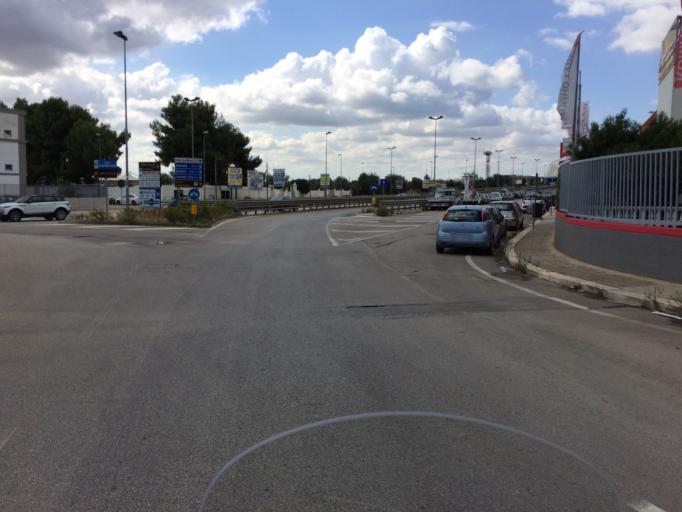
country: IT
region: Apulia
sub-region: Provincia di Bari
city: Bari
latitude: 41.1022
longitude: 16.8352
